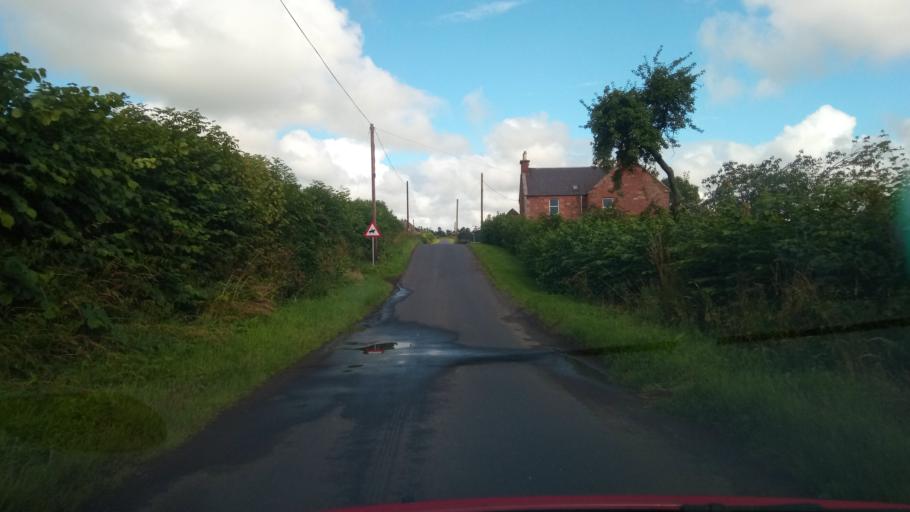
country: GB
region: Scotland
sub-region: The Scottish Borders
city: Earlston
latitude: 55.6357
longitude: -2.6918
